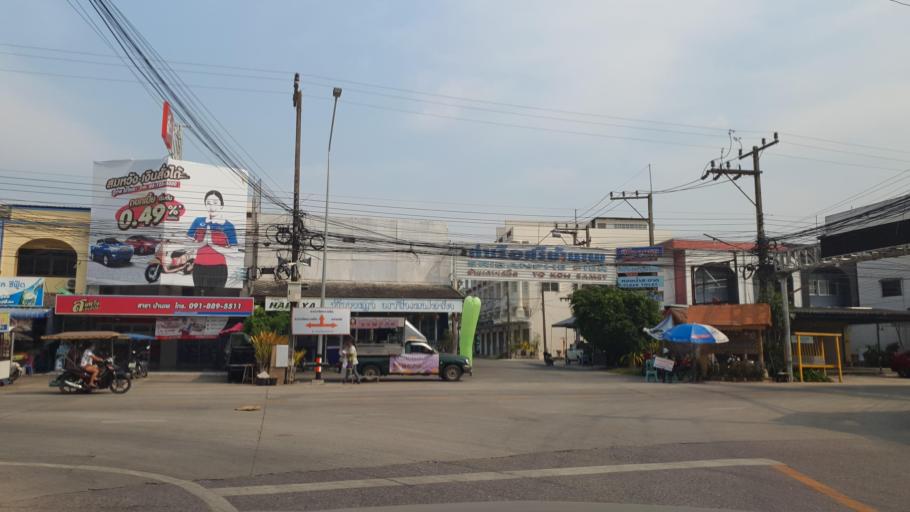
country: TH
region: Rayong
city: Rayong
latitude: 12.6253
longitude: 101.4327
